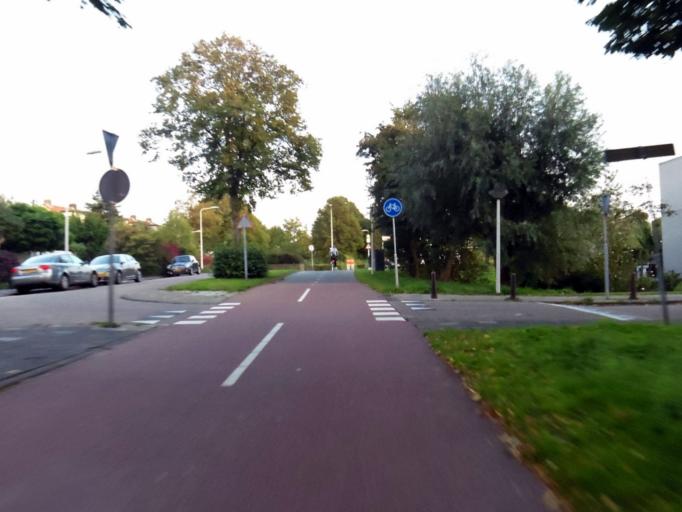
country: NL
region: South Holland
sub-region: Gemeente Voorschoten
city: Voorschoten
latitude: 52.1522
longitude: 4.4593
